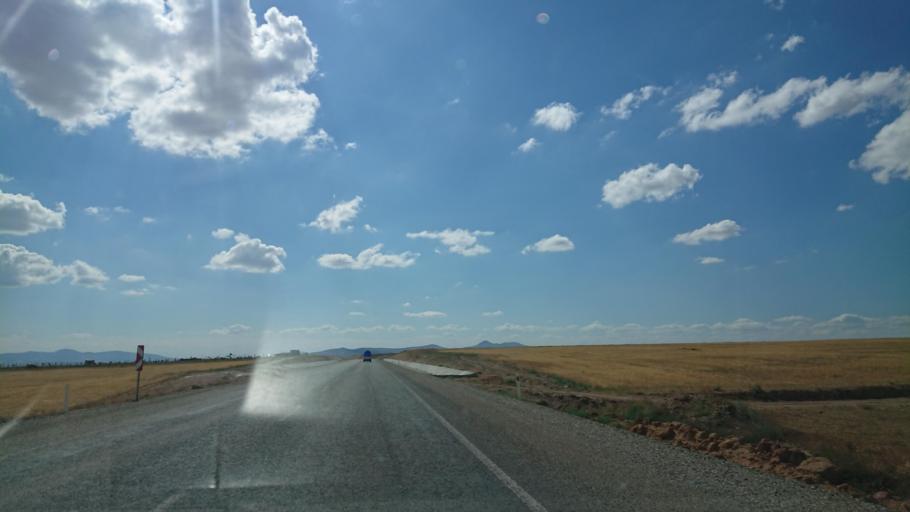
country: TR
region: Kirsehir
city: Kirsehir
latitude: 39.1231
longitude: 33.9992
